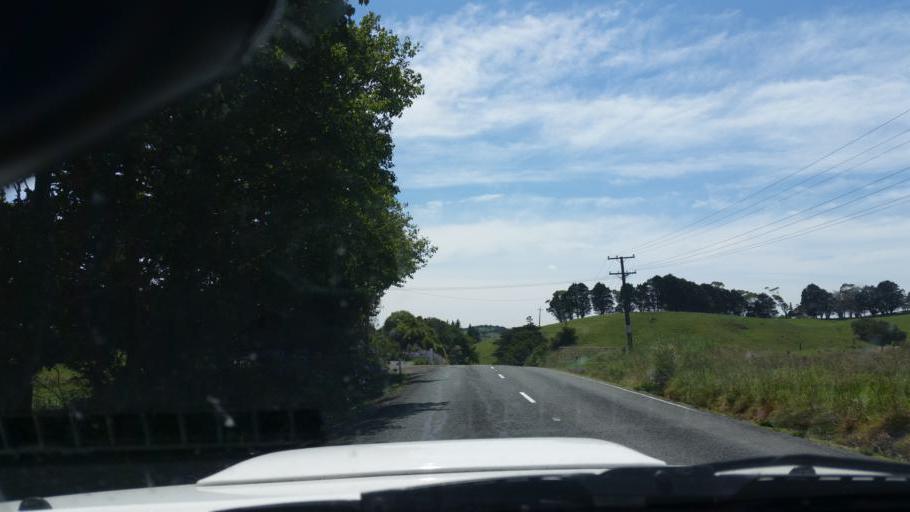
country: NZ
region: Auckland
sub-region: Auckland
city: Wellsford
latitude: -36.1645
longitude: 174.4299
